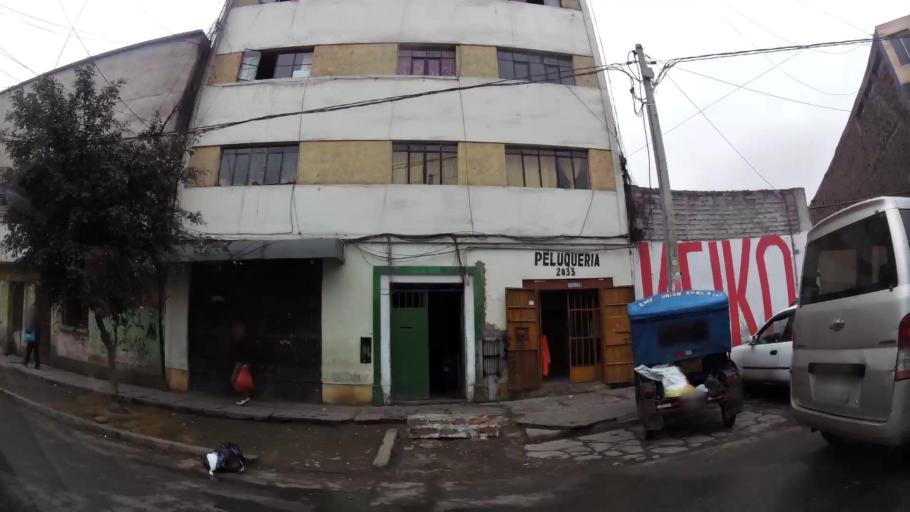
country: PE
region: Lima
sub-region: Lima
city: San Luis
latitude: -12.0686
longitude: -77.0078
